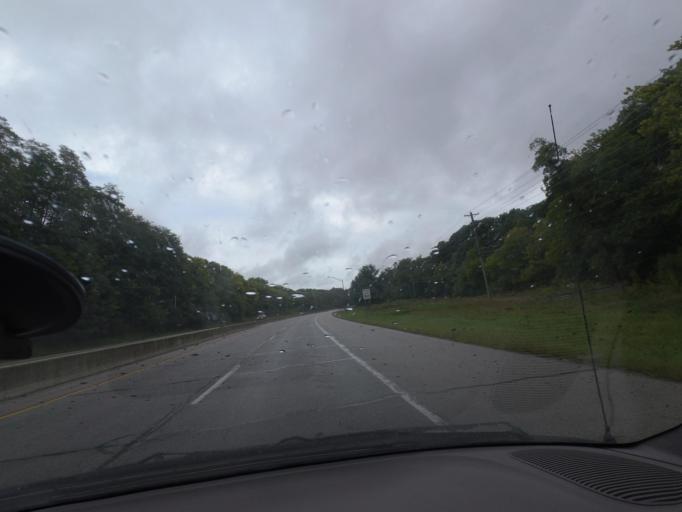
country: US
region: Indiana
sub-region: Montgomery County
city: Crawfordsville
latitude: 40.0541
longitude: -86.9055
